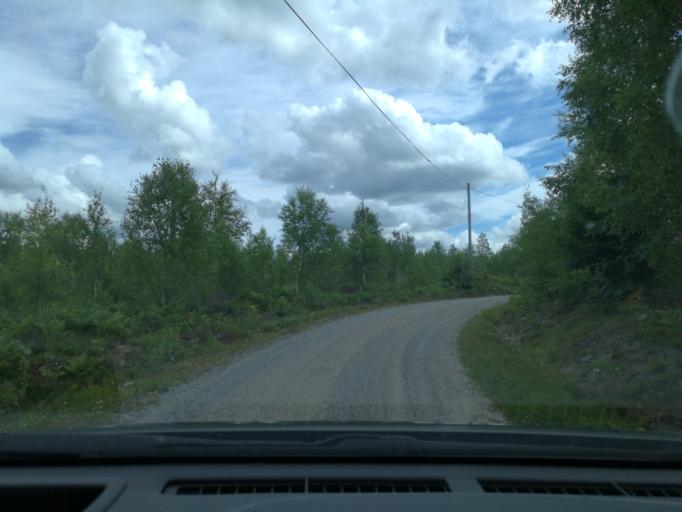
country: SE
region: Stockholm
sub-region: Sigtuna Kommun
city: Marsta
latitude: 59.6669
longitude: 17.8880
